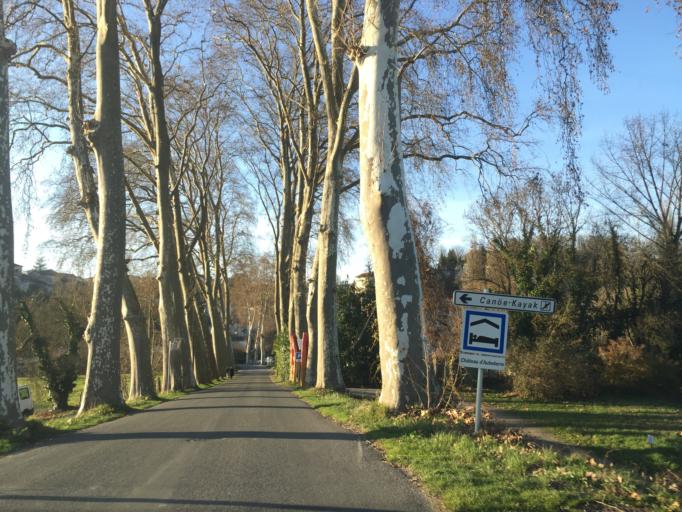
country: FR
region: Aquitaine
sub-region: Departement de la Dordogne
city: Saint-Aulaye
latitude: 45.2701
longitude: 0.1744
